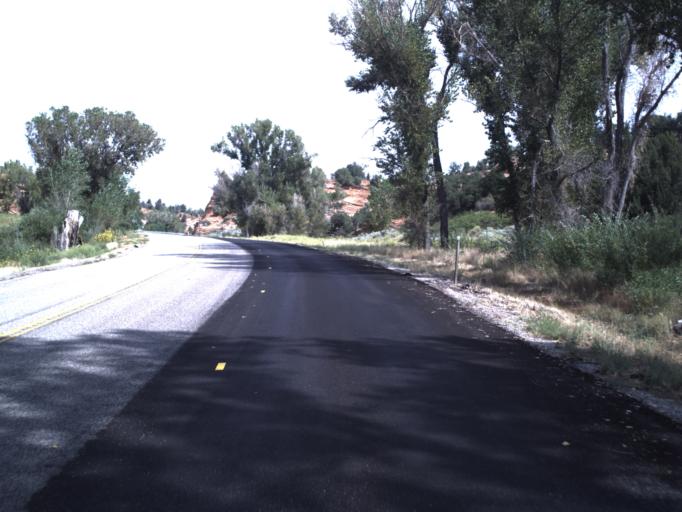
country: US
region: Utah
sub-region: Kane County
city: Kanab
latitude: 37.1296
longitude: -112.5648
